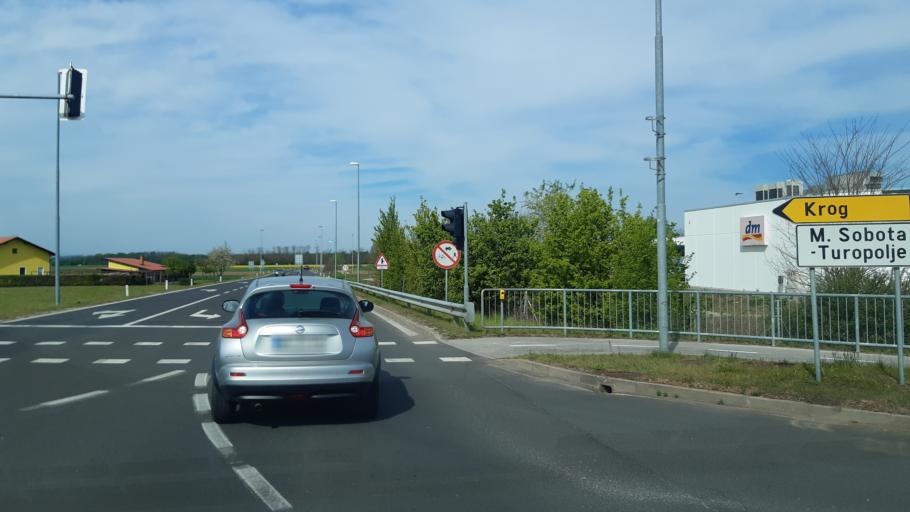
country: SI
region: Murska Sobota
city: Krog
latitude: 46.6478
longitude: 16.1487
